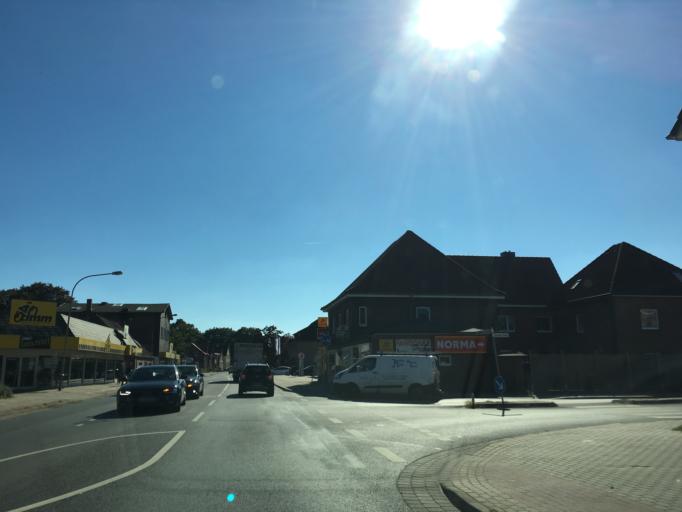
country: DE
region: Lower Saxony
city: Winsen
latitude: 53.3526
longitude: 10.2068
